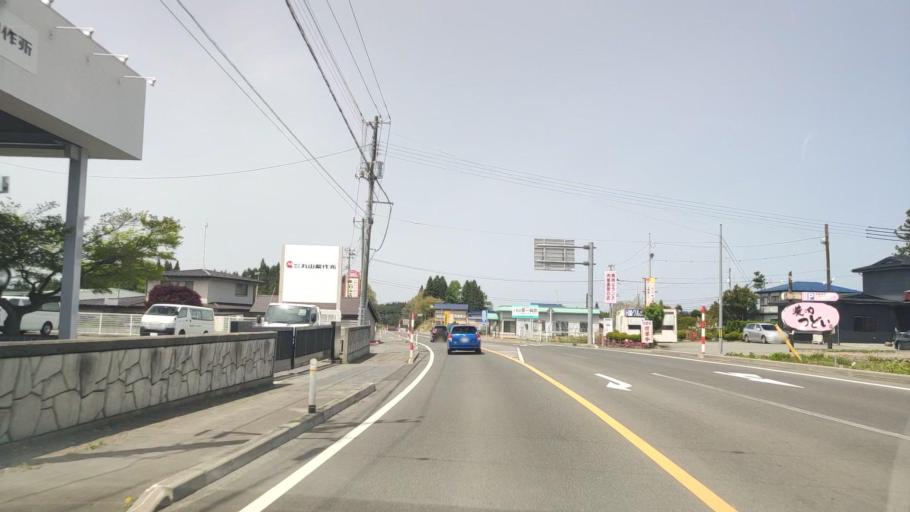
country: JP
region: Aomori
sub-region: Misawa Shi
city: Inuotose
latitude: 40.6587
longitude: 141.1918
